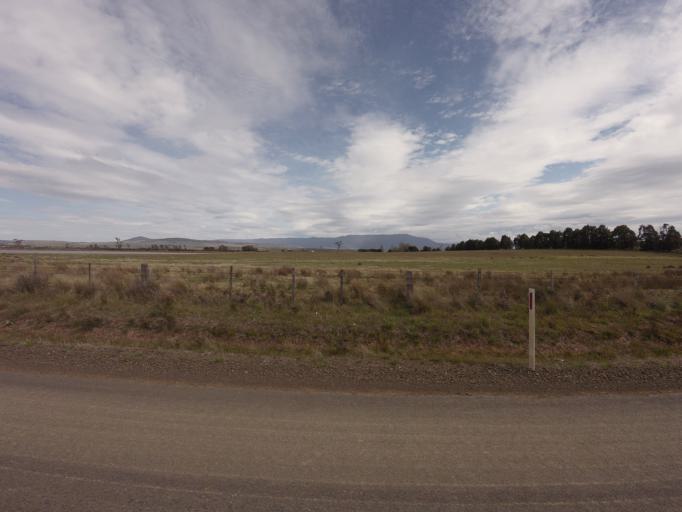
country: AU
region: Tasmania
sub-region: Northern Midlands
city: Evandale
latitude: -41.8266
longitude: 147.3209
